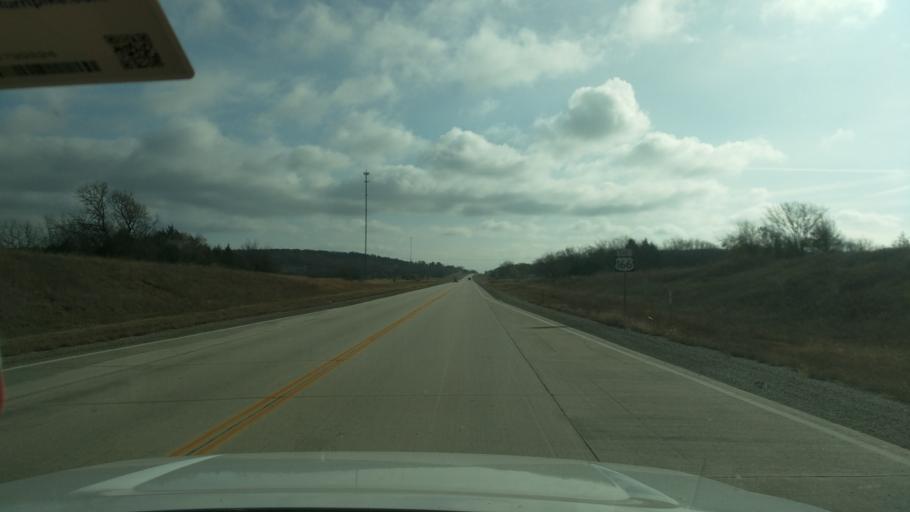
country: US
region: Kansas
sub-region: Chautauqua County
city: Sedan
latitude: 37.0795
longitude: -96.1002
